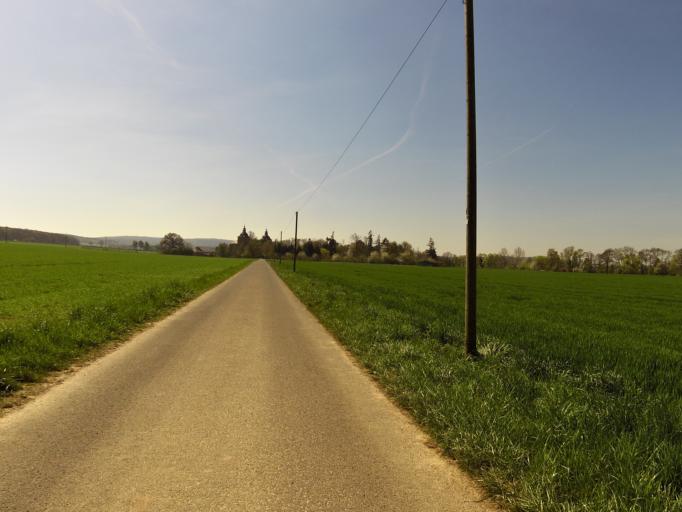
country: DE
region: North Rhine-Westphalia
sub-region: Regierungsbezirk Koln
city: Rheinbach
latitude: 50.6262
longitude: 6.8729
